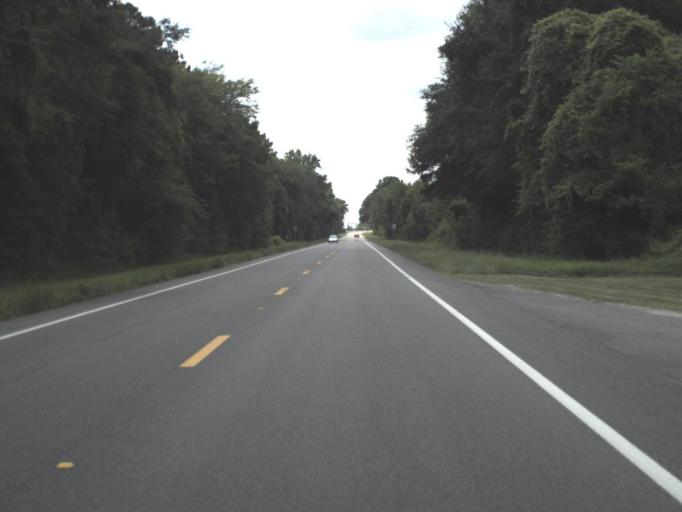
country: US
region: Florida
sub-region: Hamilton County
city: Jasper
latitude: 30.4841
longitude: -82.9232
